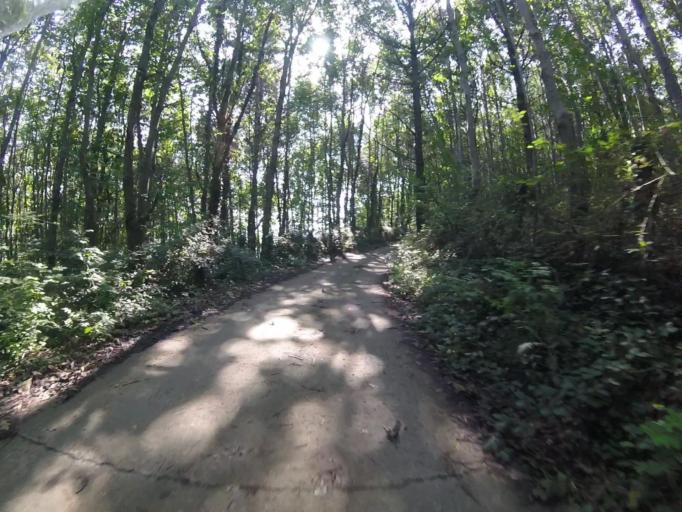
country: ES
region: Basque Country
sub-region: Provincia de Guipuzcoa
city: Irun
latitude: 43.3292
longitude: -1.7613
